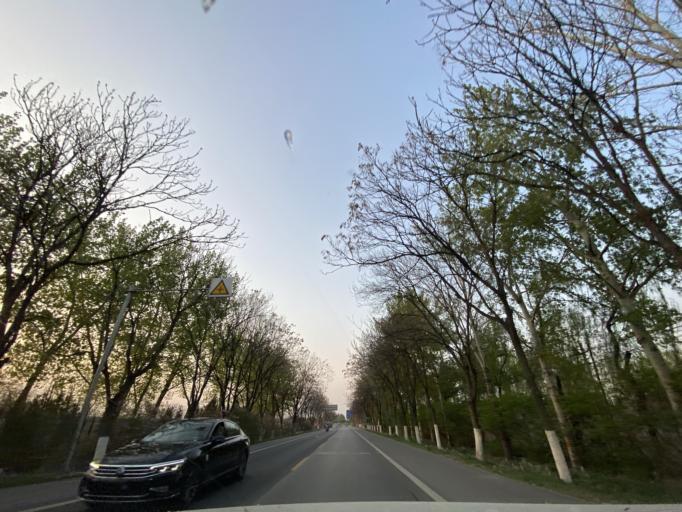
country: CN
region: Beijing
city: Weishanzhuang
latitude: 39.6120
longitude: 116.4096
